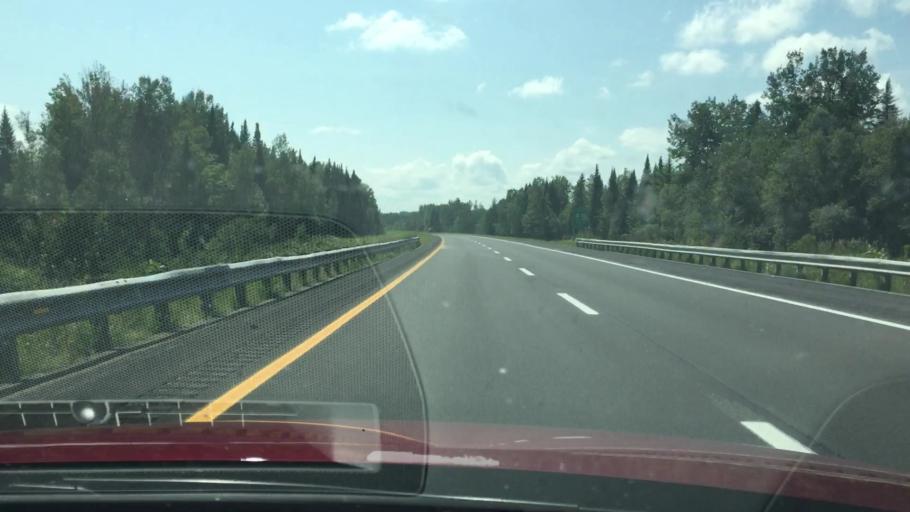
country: US
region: Maine
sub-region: Penobscot County
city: Patten
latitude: 45.8915
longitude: -68.4030
